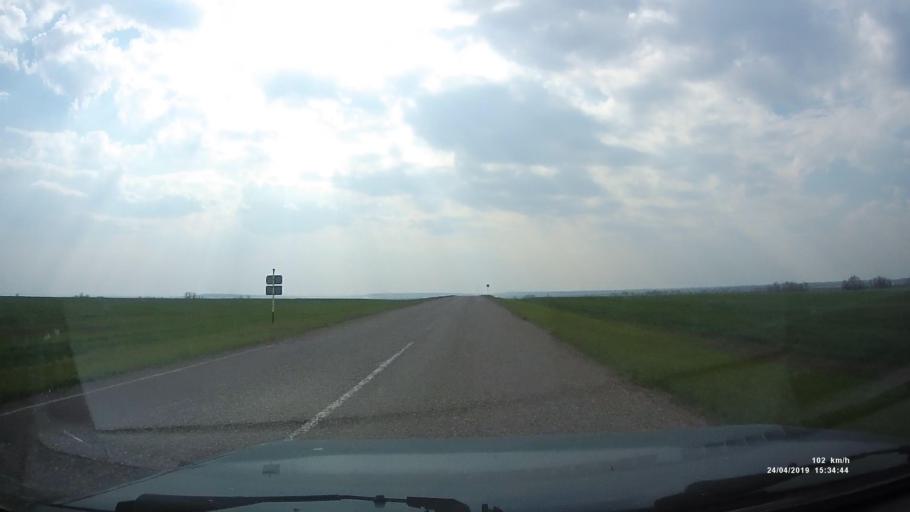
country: RU
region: Kalmykiya
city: Yashalta
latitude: 46.5995
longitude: 42.9076
